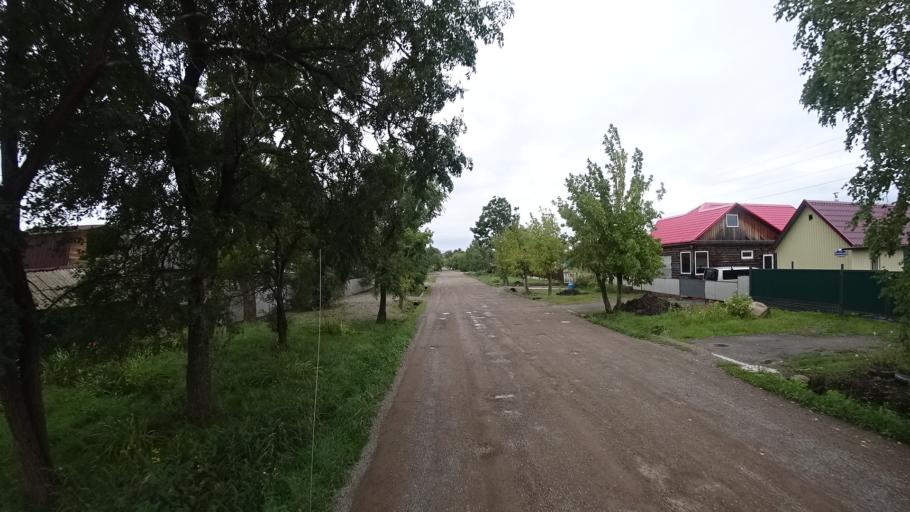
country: RU
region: Primorskiy
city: Chernigovka
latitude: 44.3425
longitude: 132.5656
